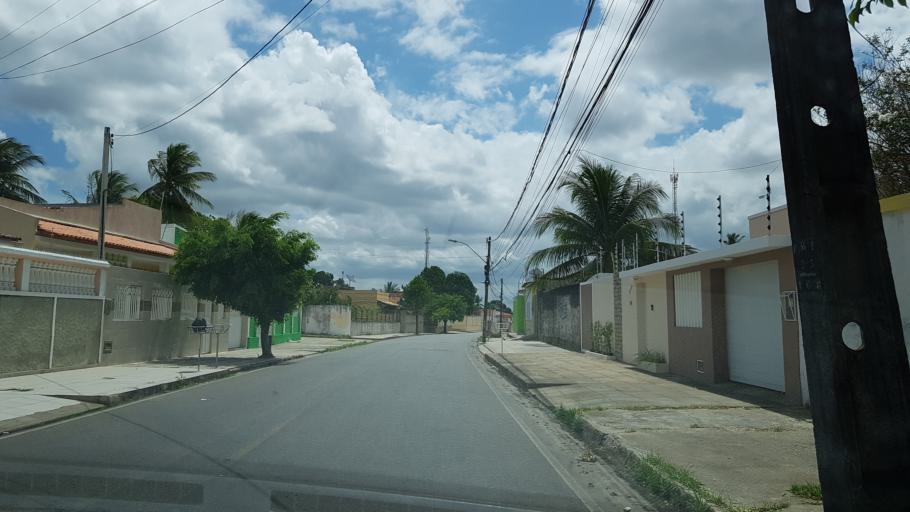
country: BR
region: Alagoas
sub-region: Penedo
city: Penedo
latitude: -10.2809
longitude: -36.5669
